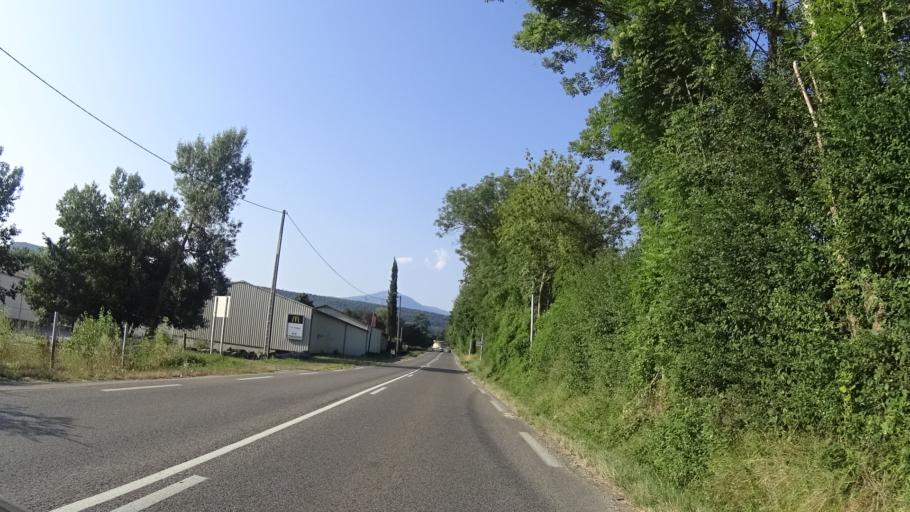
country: FR
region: Midi-Pyrenees
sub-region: Departement de l'Ariege
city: Lavelanet
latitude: 42.9537
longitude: 1.8605
